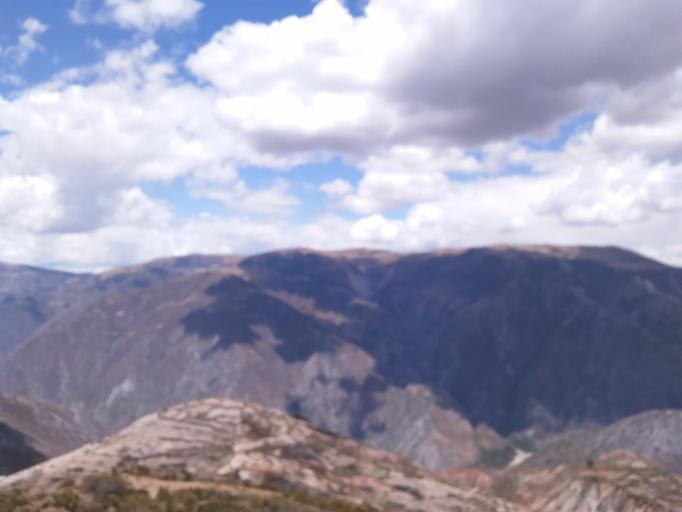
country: PE
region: Ayacucho
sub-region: Provincia de Victor Fajardo
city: Canaria
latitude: -13.8847
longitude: -73.9376
